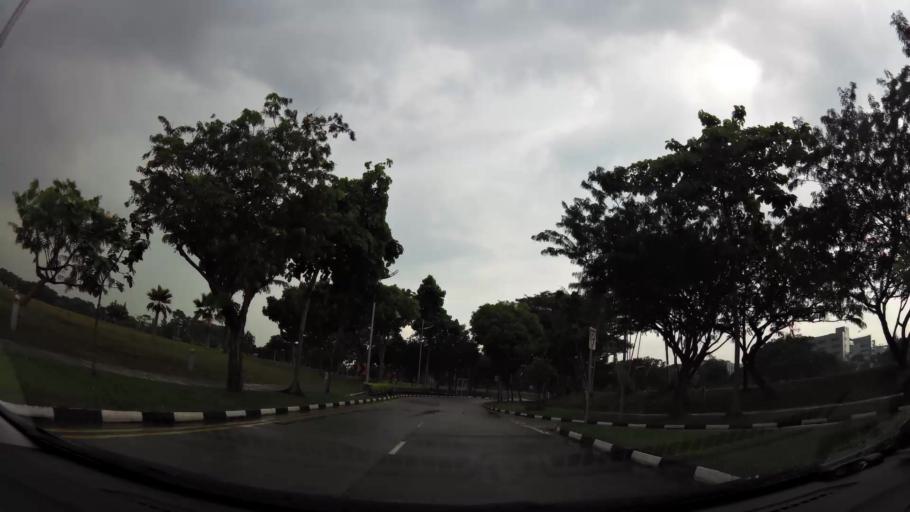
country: SG
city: Singapore
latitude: 1.3405
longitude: 103.9685
